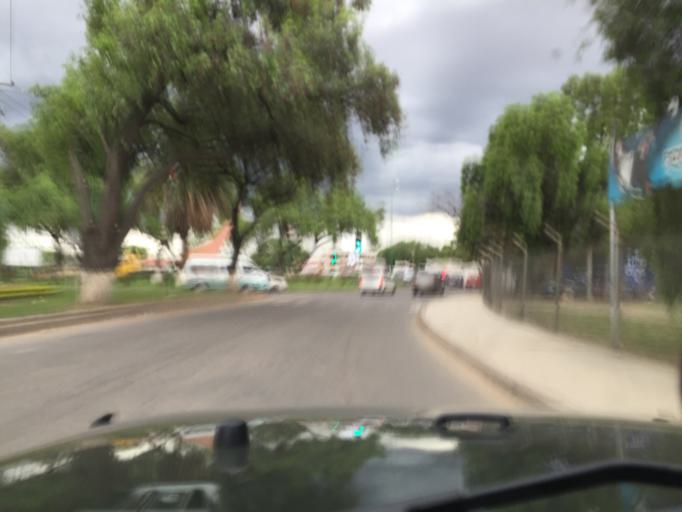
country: BO
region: Cochabamba
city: Cochabamba
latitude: -17.4100
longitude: -66.1731
